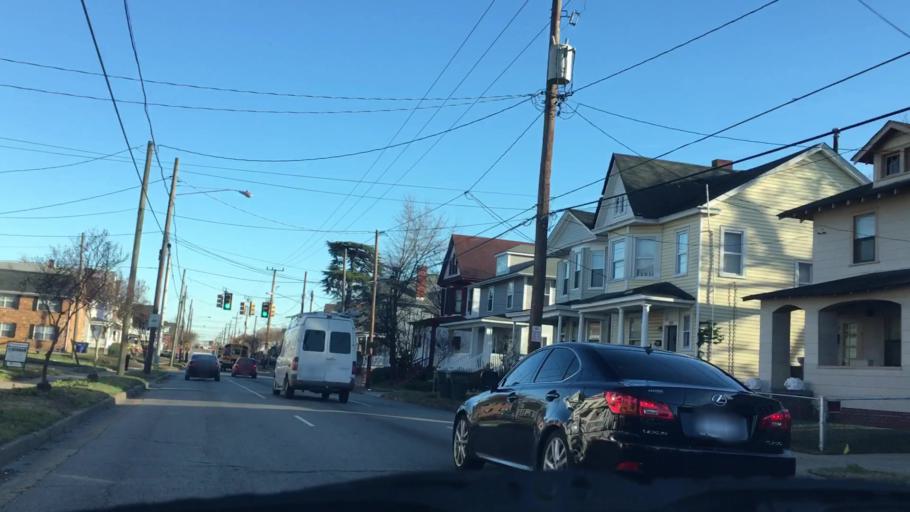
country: US
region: Virginia
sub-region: City of Norfolk
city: Norfolk
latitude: 36.8723
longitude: -76.2877
